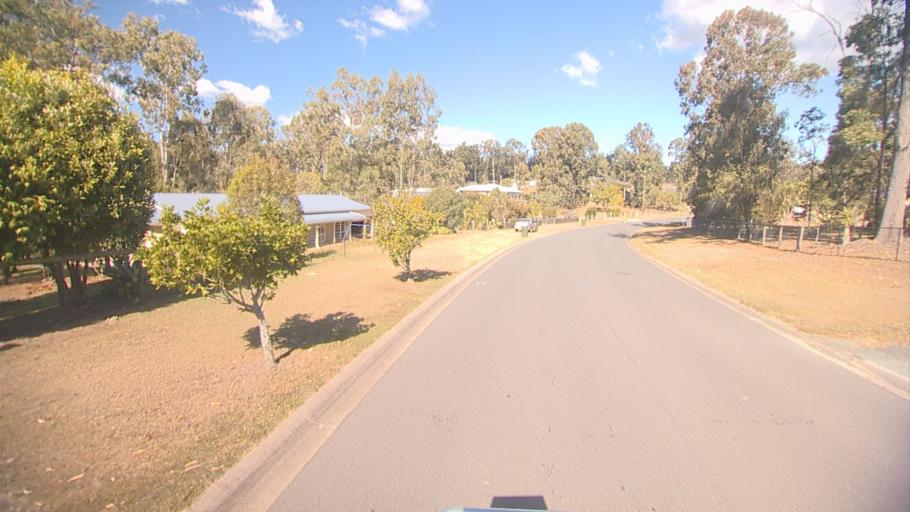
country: AU
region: Queensland
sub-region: Logan
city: North Maclean
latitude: -27.7522
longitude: 152.9412
